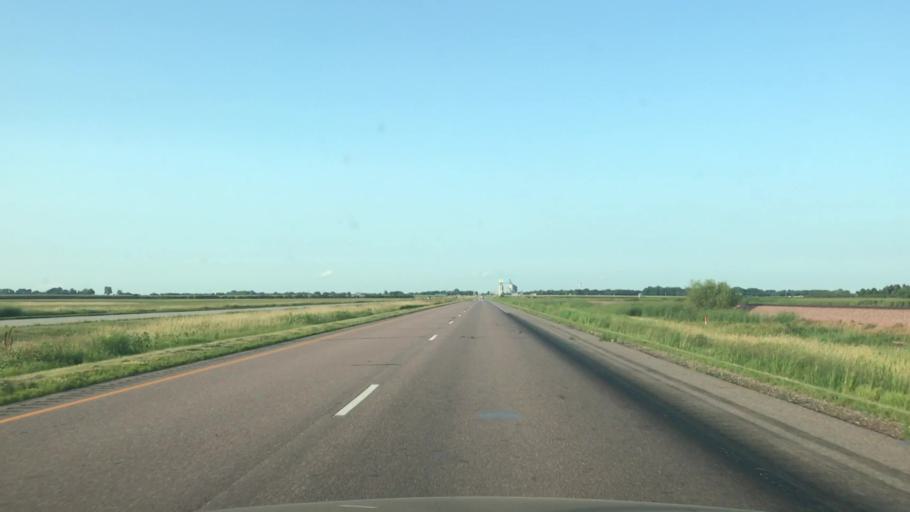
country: US
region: Minnesota
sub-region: Jackson County
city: Lakefield
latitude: 43.7784
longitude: -95.3485
